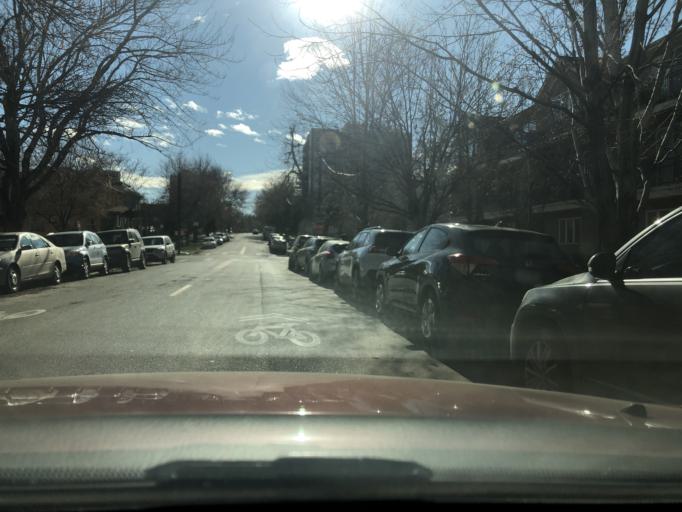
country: US
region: Colorado
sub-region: Denver County
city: Denver
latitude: 39.7422
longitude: -104.9685
